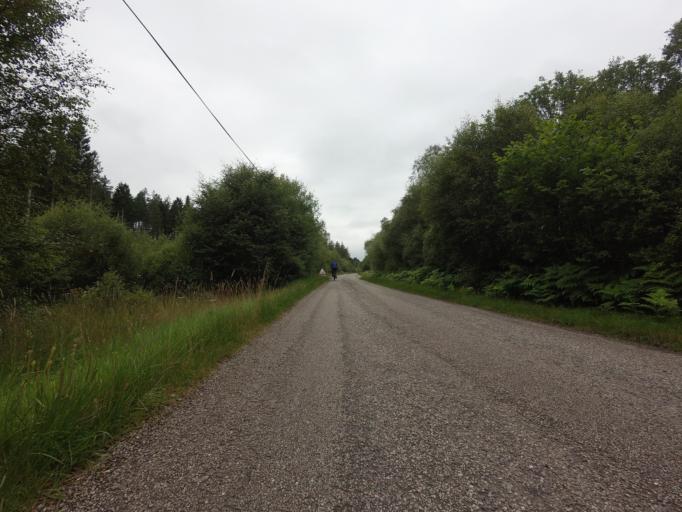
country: GB
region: Scotland
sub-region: Highland
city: Evanton
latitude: 57.9713
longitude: -4.4133
